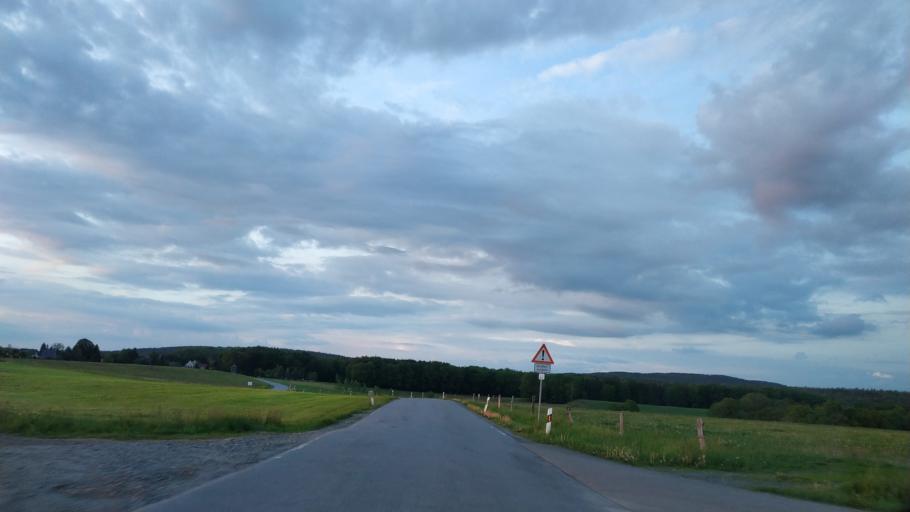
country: DE
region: Saxony
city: Lohmen
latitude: 50.9799
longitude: 14.0224
